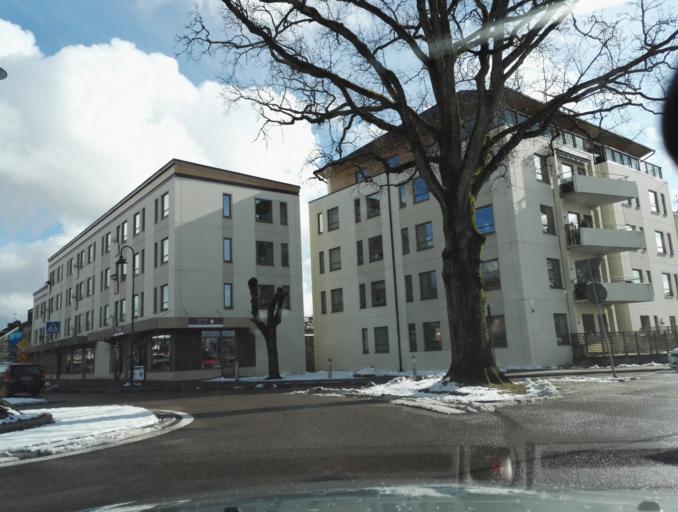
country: SE
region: Vaestra Goetaland
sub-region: Bollebygds Kommun
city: Bollebygd
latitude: 57.6689
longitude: 12.5671
